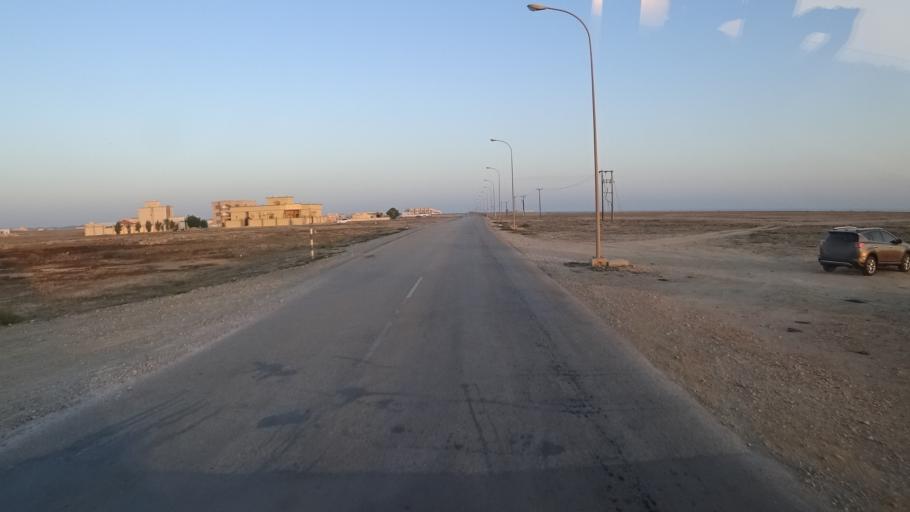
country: OM
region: Zufar
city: Salalah
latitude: 16.9793
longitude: 54.7089
